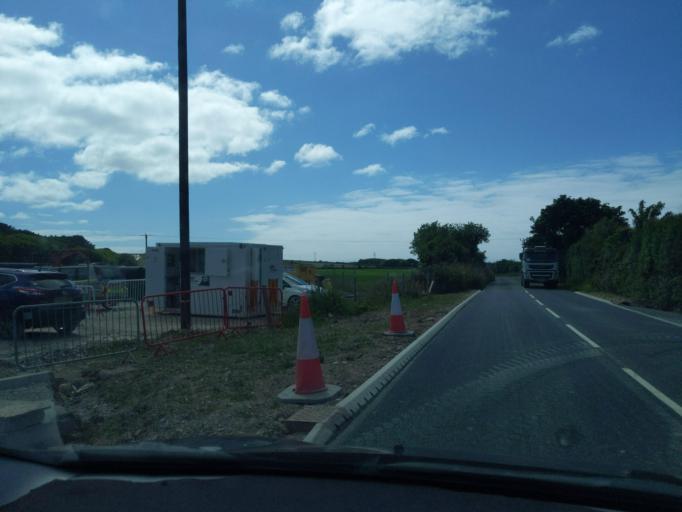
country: GB
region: England
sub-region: Cornwall
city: Perranporth
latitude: 50.2968
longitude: -5.1287
